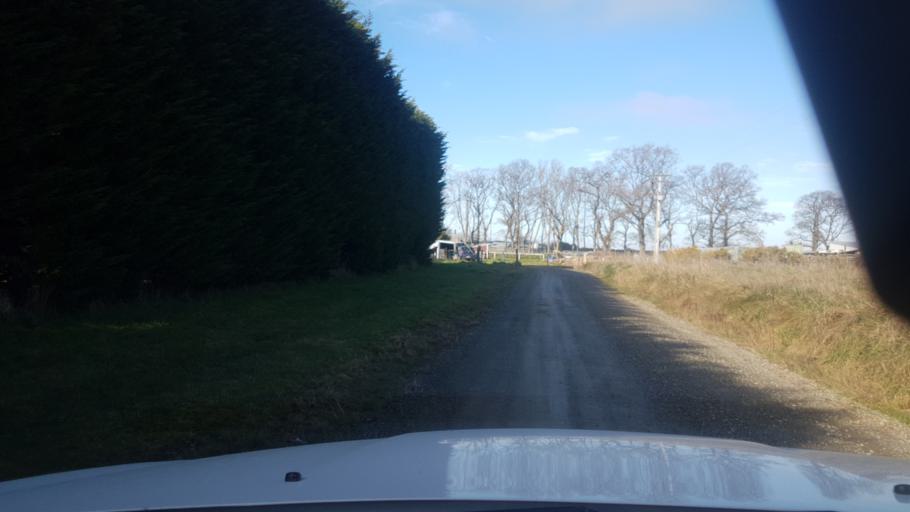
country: NZ
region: Canterbury
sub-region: Timaru District
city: Timaru
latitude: -44.3296
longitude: 171.2522
